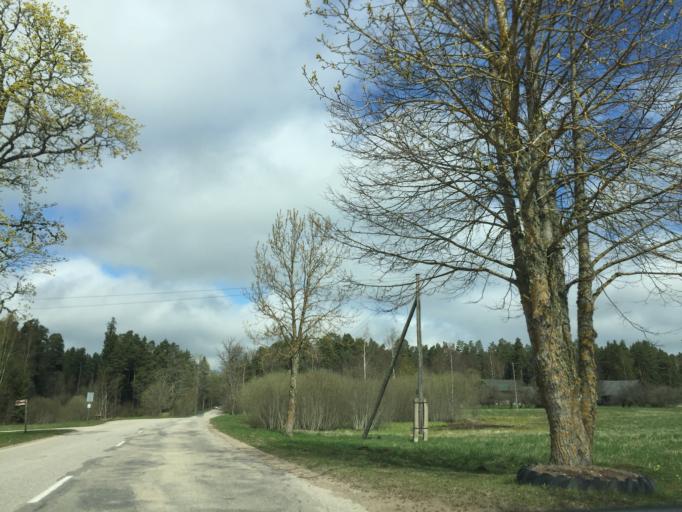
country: LV
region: Apes Novads
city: Ape
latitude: 57.5021
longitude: 26.4011
